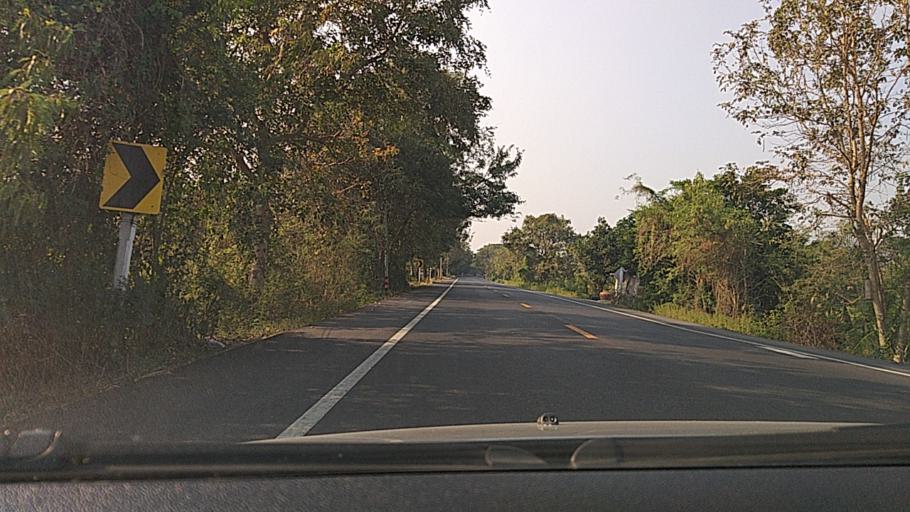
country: TH
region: Sing Buri
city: Phrom Buri
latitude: 14.7540
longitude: 100.4373
